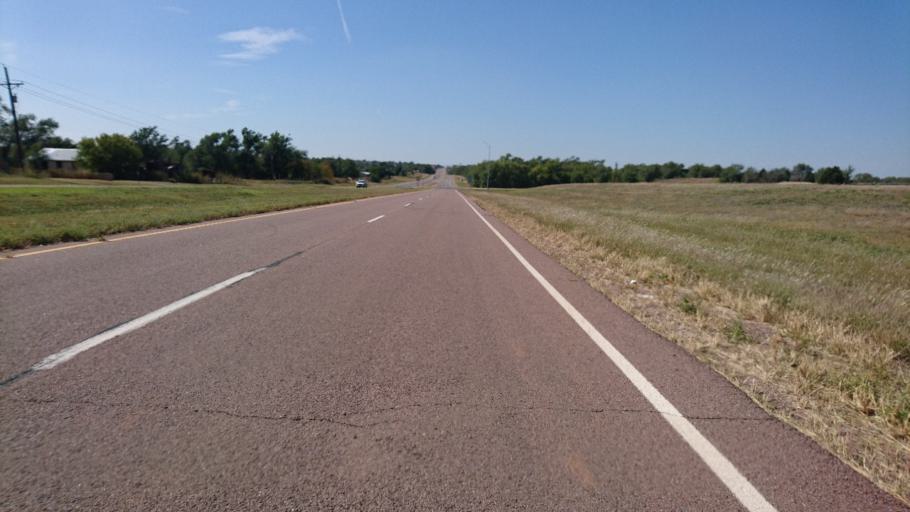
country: US
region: Texas
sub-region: Wheeler County
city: Shamrock
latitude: 35.2267
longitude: -100.2250
